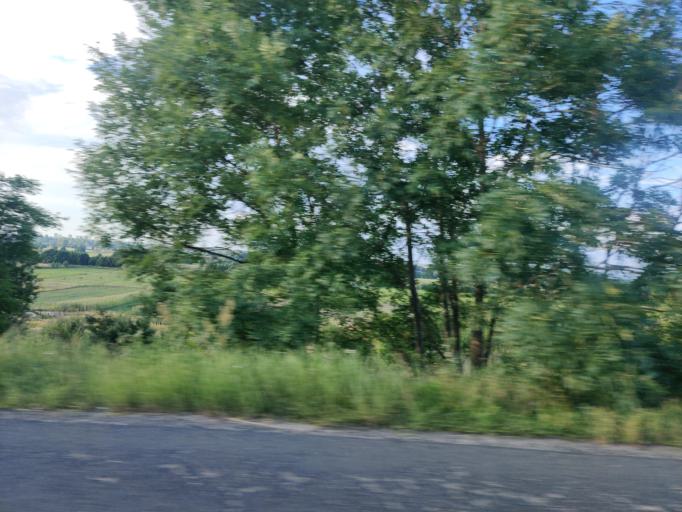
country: PL
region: Greater Poland Voivodeship
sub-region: Konin
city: Konin
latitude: 52.2005
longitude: 18.2852
